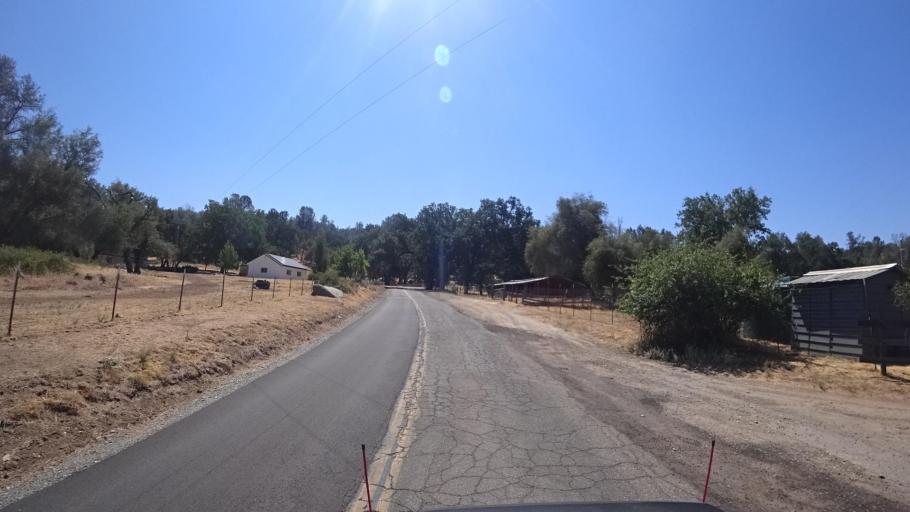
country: US
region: California
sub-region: Mariposa County
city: Mariposa
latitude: 37.4193
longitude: -119.9660
